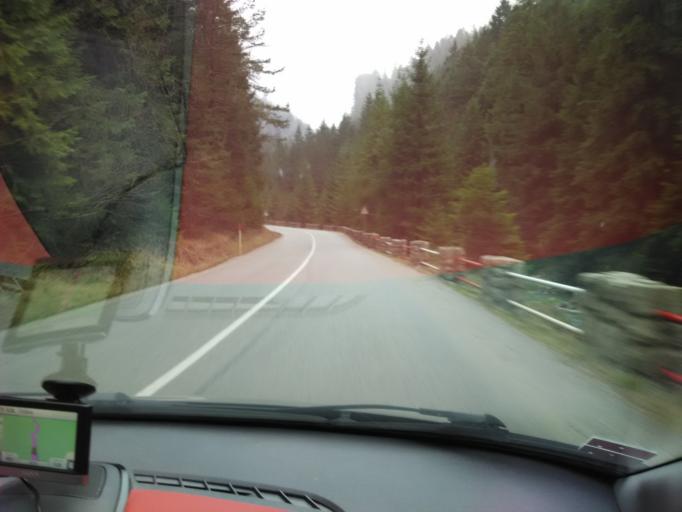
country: SK
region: Zilinsky
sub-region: Okres Zilina
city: Terchova
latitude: 49.2490
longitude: 19.0386
